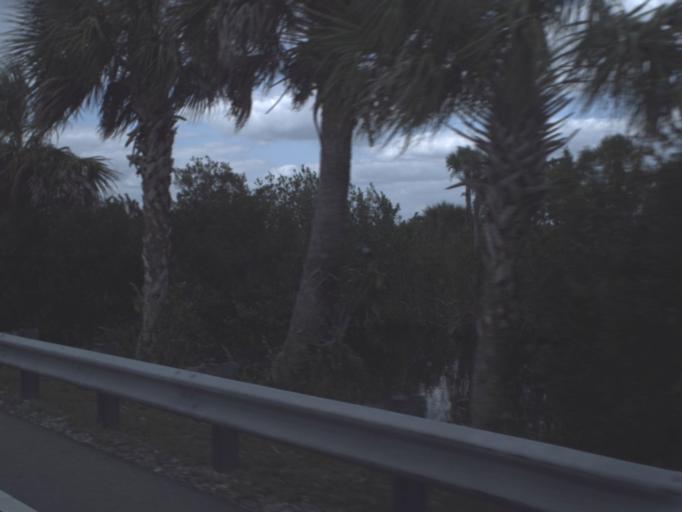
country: US
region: Florida
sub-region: Collier County
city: Marco
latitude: 25.9532
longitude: -81.4853
